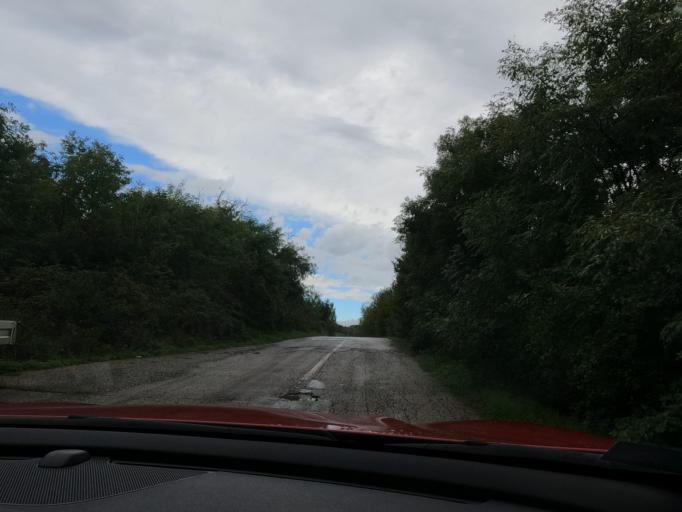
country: HR
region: Sisacko-Moslavacka
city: Glina
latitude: 45.3016
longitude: 16.1684
